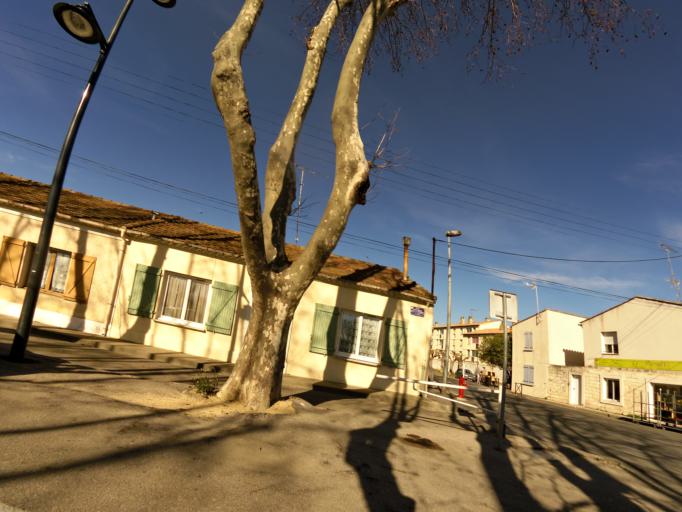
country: FR
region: Languedoc-Roussillon
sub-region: Departement du Gard
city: Aigues-Mortes
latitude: 43.5681
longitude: 4.1971
